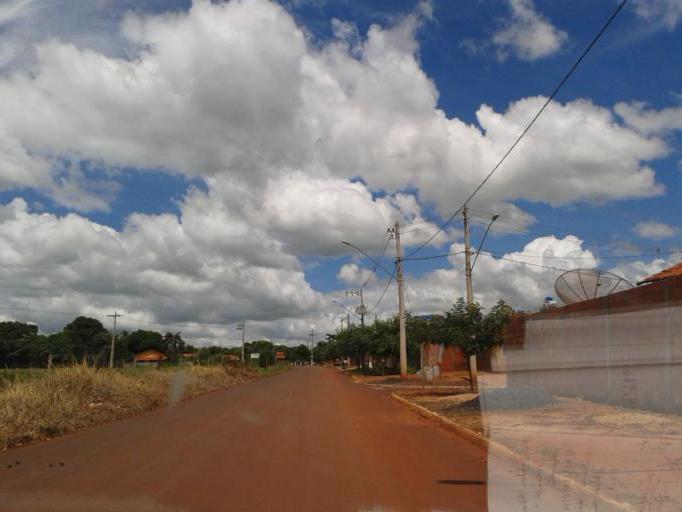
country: BR
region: Minas Gerais
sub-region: Santa Vitoria
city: Santa Vitoria
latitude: -18.8373
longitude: -50.1160
